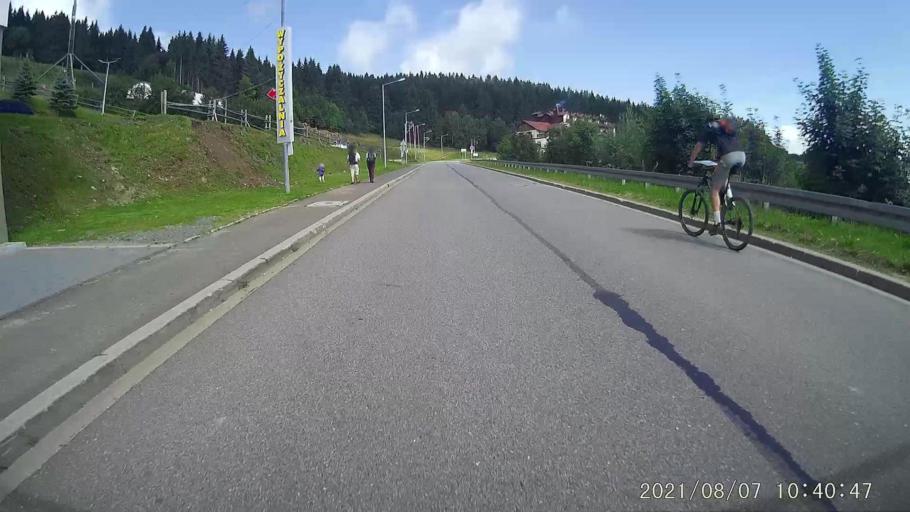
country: PL
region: Lower Silesian Voivodeship
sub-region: Powiat klodzki
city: Duszniki-Zdroj
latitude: 50.3416
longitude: 16.3822
